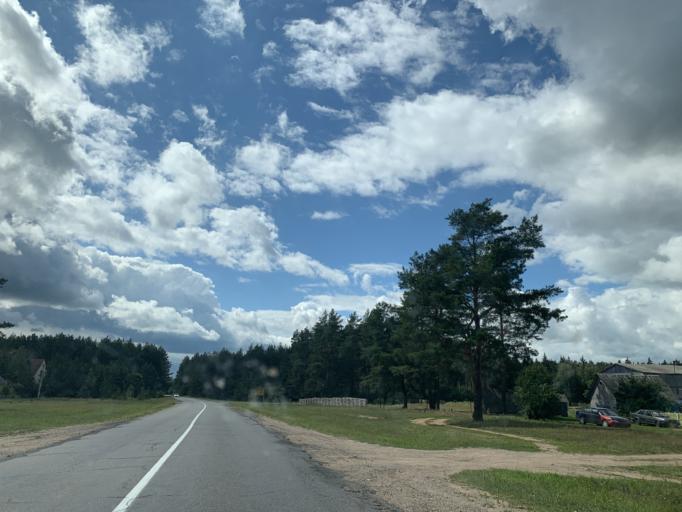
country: BY
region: Minsk
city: Rakaw
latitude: 53.9868
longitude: 26.9452
